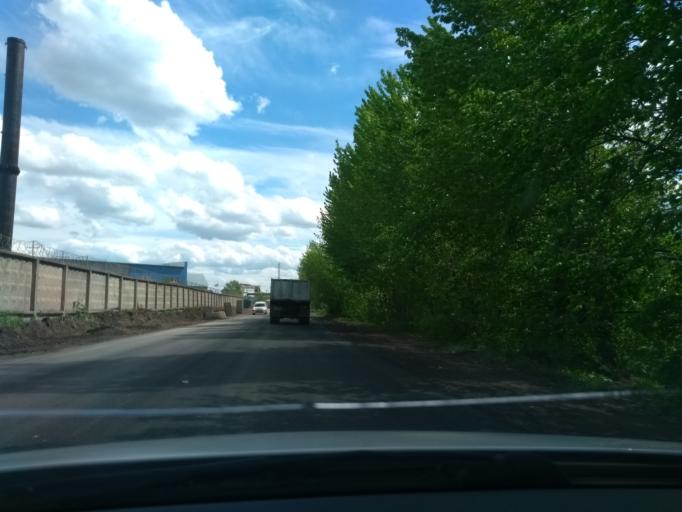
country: RU
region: Perm
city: Kondratovo
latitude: 58.0124
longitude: 56.0622
